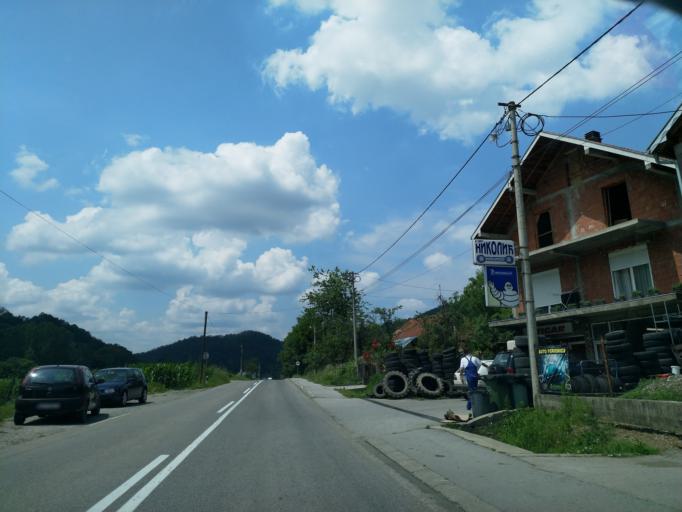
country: RS
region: Central Serbia
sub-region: Rasinski Okrug
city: Aleksandrovac
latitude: 43.3677
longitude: 21.0586
